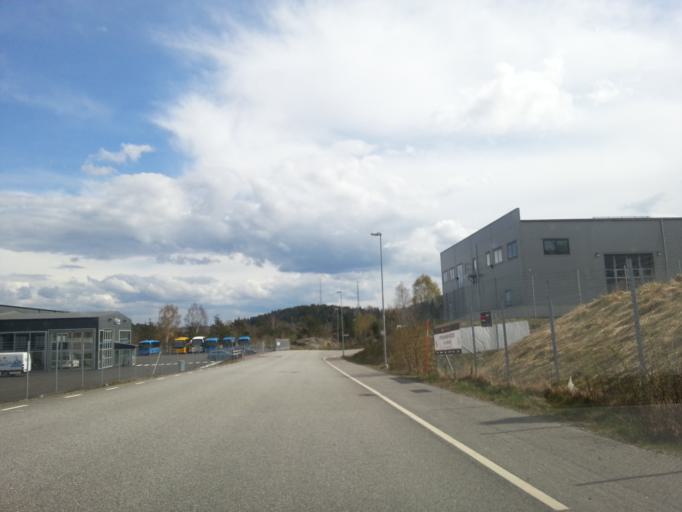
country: SE
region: Vaestra Goetaland
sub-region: Kungalvs Kommun
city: Kungalv
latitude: 57.8836
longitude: 11.9396
